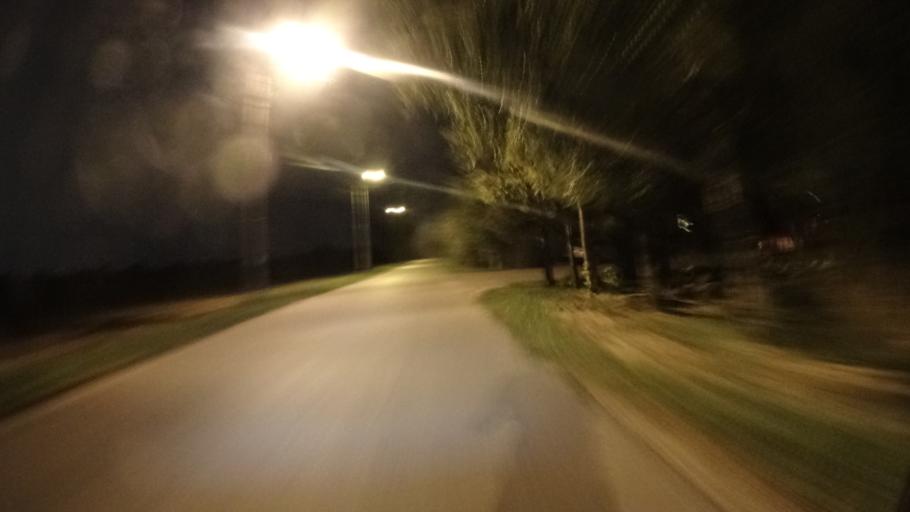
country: PL
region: Masovian Voivodeship
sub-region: Powiat warszawski zachodni
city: Ozarow Mazowiecki
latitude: 52.2457
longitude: 20.7864
